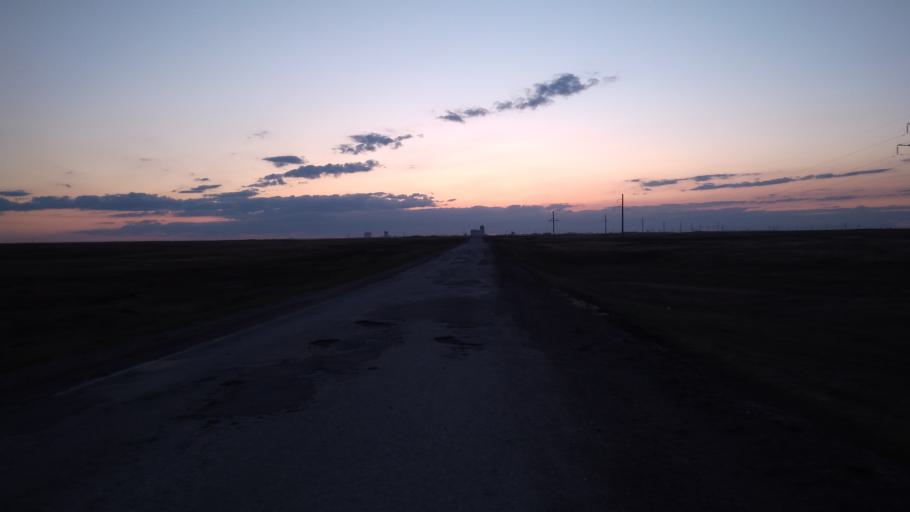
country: RU
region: Chelyabinsk
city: Troitsk
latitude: 54.0914
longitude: 61.6435
